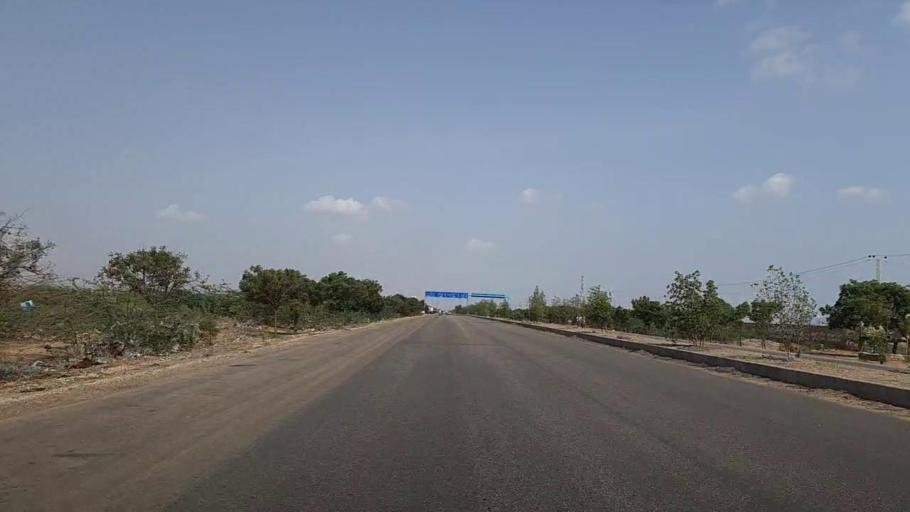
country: PK
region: Sindh
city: Malir Cantonment
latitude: 24.8616
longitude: 67.3956
